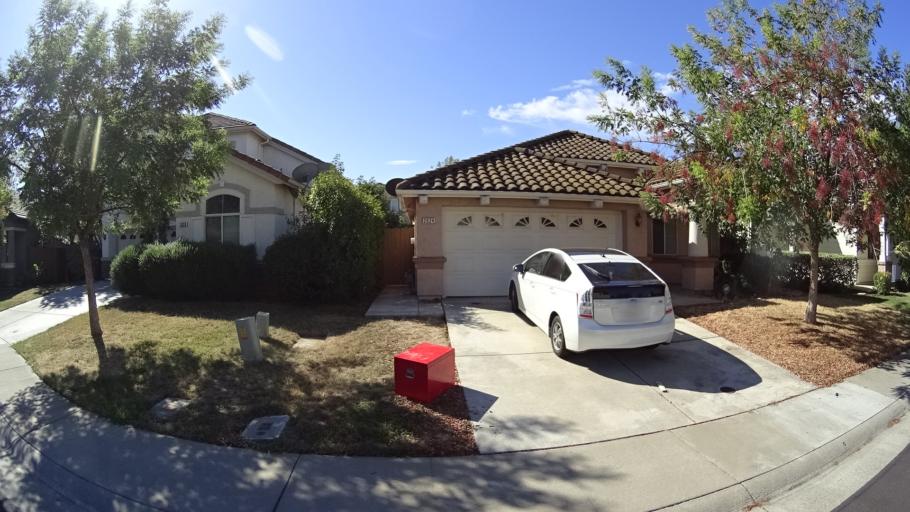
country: US
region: California
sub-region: Sacramento County
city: Laguna
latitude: 38.4260
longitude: -121.4763
